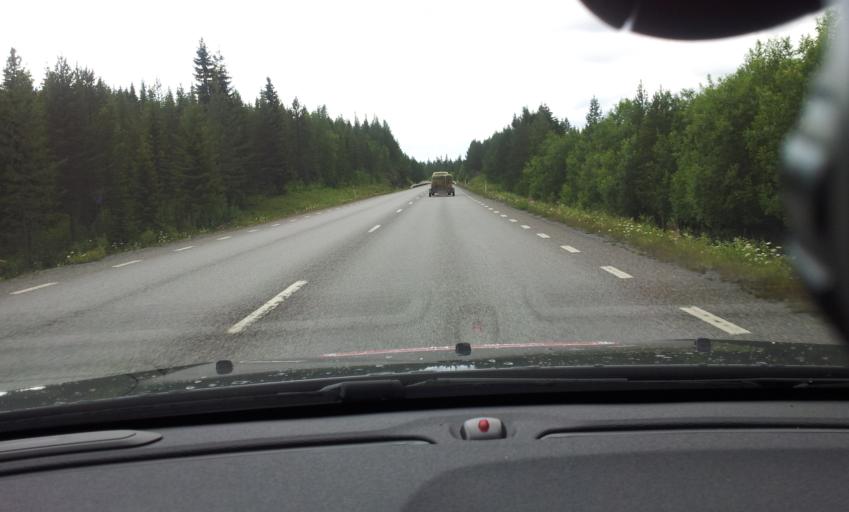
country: SE
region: Jaemtland
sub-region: Krokoms Kommun
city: Valla
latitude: 63.3127
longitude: 13.7332
